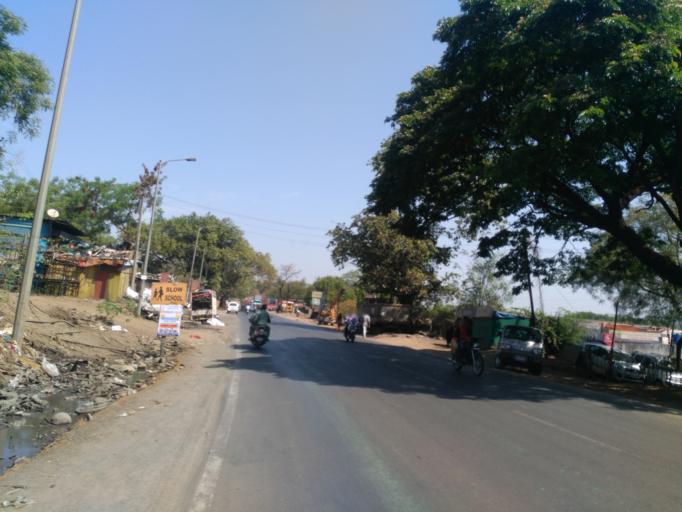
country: IN
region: Maharashtra
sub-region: Pune Division
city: Pune
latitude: 18.4394
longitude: 73.8603
